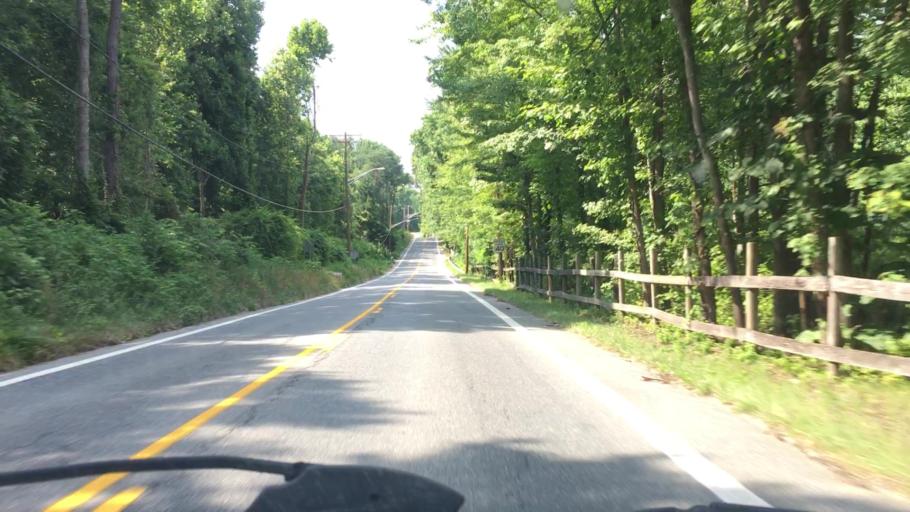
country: US
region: Maryland
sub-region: Prince George's County
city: Glenn Dale
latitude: 39.0142
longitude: -76.7824
